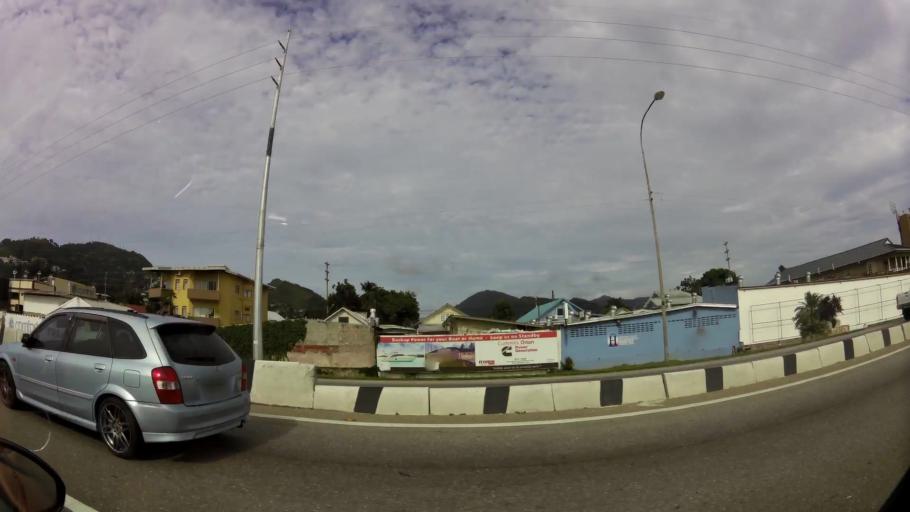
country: TT
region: City of Port of Spain
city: Mucurapo
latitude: 10.6703
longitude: -61.5387
